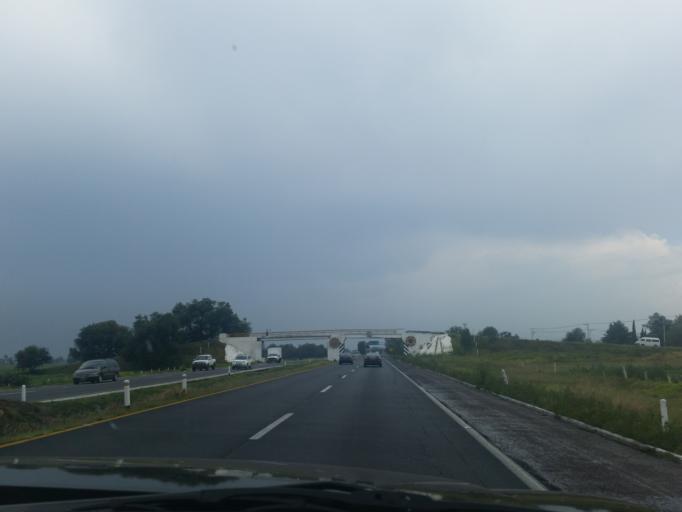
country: MX
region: Mexico
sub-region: Acolman de Nezahualcoyotl
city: San Pedro Tepetitlan
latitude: 19.6340
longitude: -98.9067
